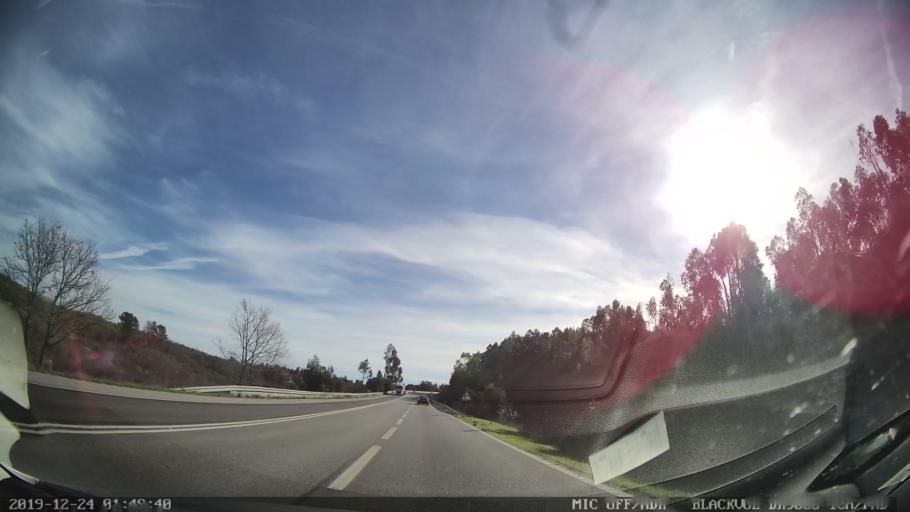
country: PT
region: Portalegre
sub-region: Nisa
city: Nisa
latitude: 39.5047
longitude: -7.7705
